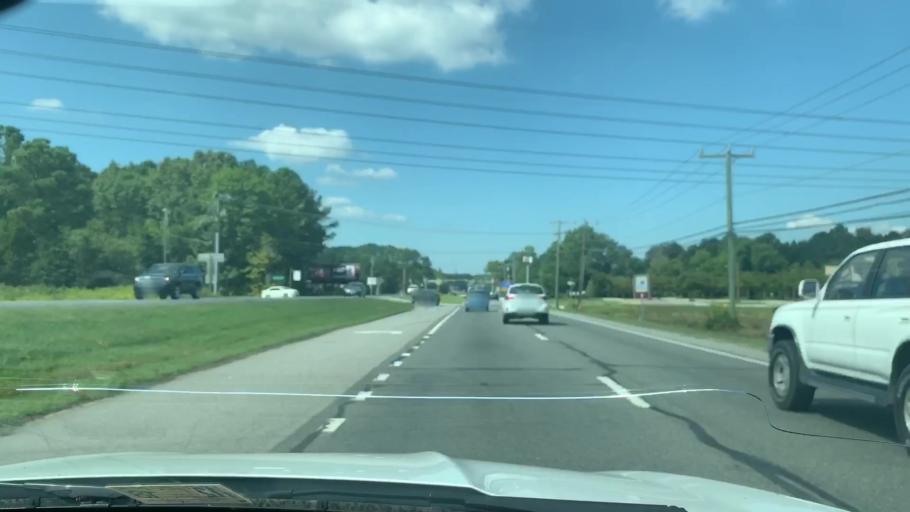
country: US
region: Virginia
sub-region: York County
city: Yorktown
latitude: 37.1750
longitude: -76.4767
